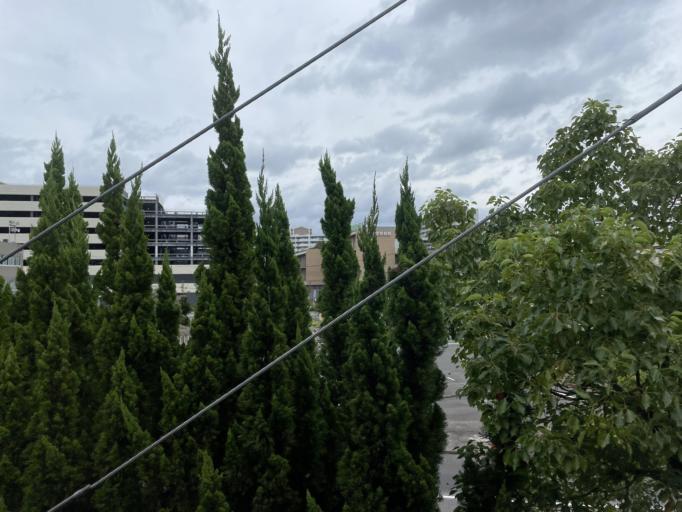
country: JP
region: Hyogo
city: Nishinomiya-hama
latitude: 34.7418
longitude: 135.3574
